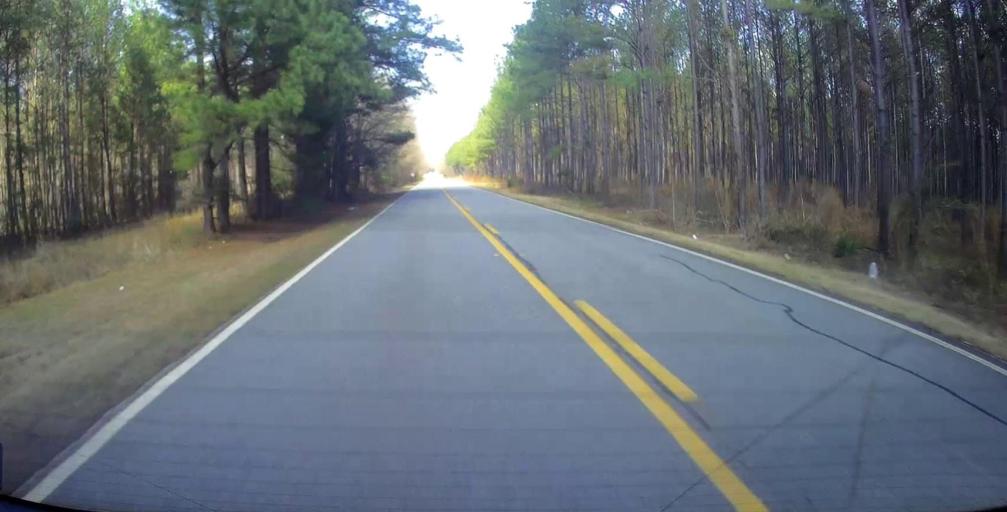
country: US
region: Georgia
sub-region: Twiggs County
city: Jeffersonville
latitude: 32.7637
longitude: -83.3415
